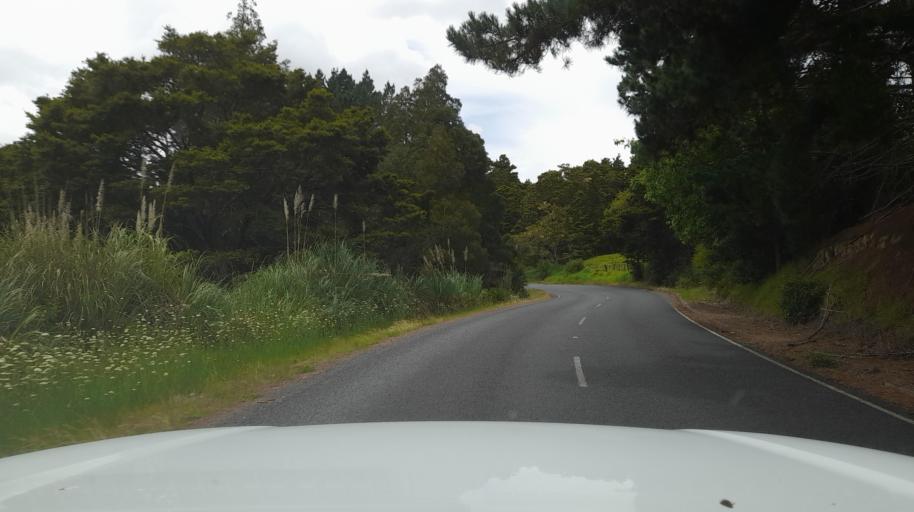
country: NZ
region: Northland
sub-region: Far North District
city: Kaitaia
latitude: -35.3583
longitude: 173.4858
